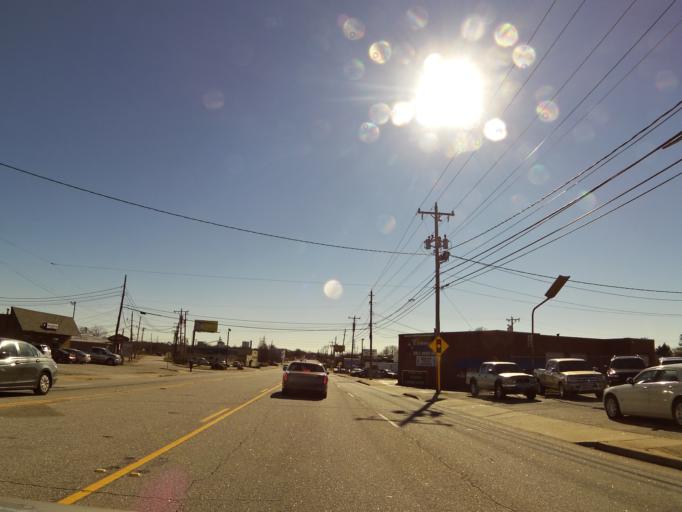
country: US
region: South Carolina
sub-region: Greenville County
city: Sans Souci
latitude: 34.8828
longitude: -82.4050
